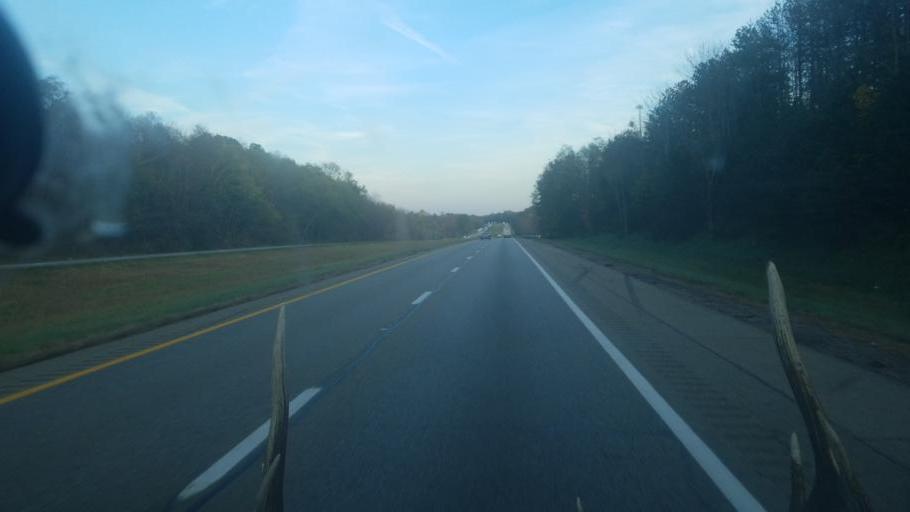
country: US
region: Ohio
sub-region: Muskingum County
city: Zanesville
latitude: 39.9449
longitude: -82.1054
